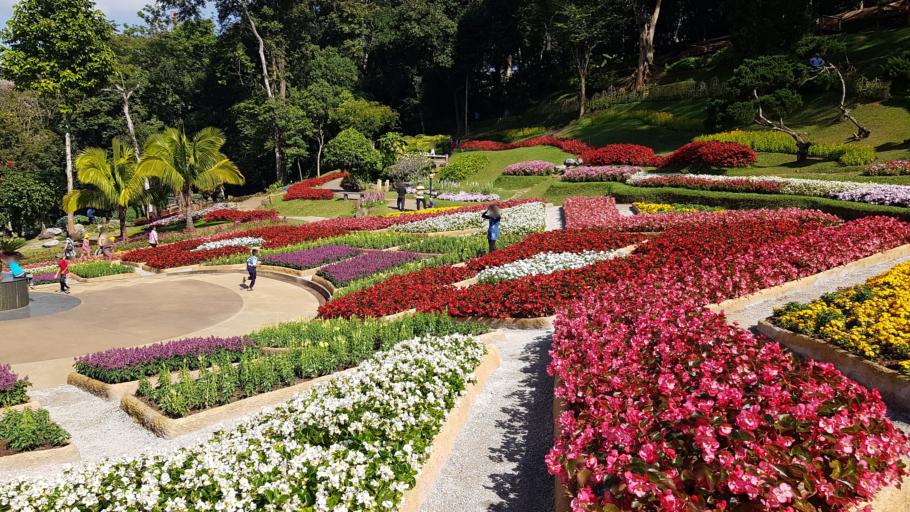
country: TH
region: Chiang Rai
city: Mae Fa Luang
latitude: 20.2882
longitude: 99.8097
